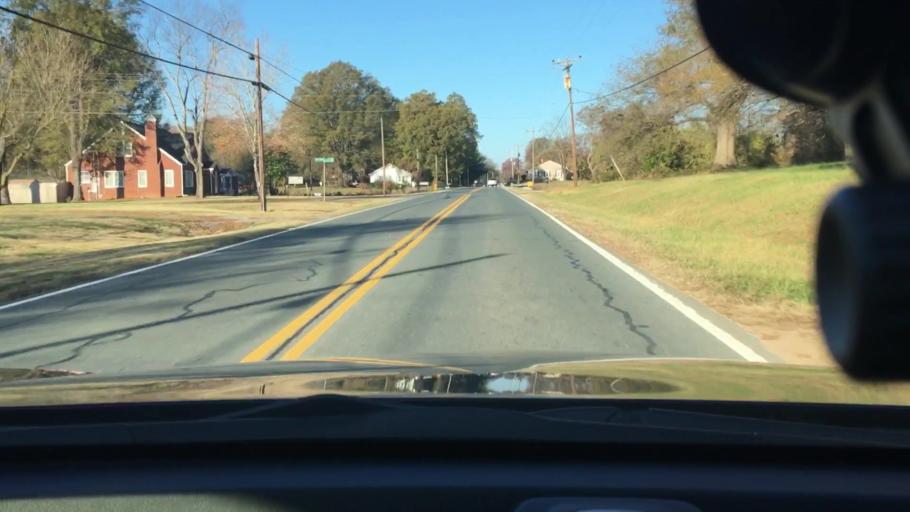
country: US
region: North Carolina
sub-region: Stanly County
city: Albemarle
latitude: 35.3699
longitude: -80.2761
